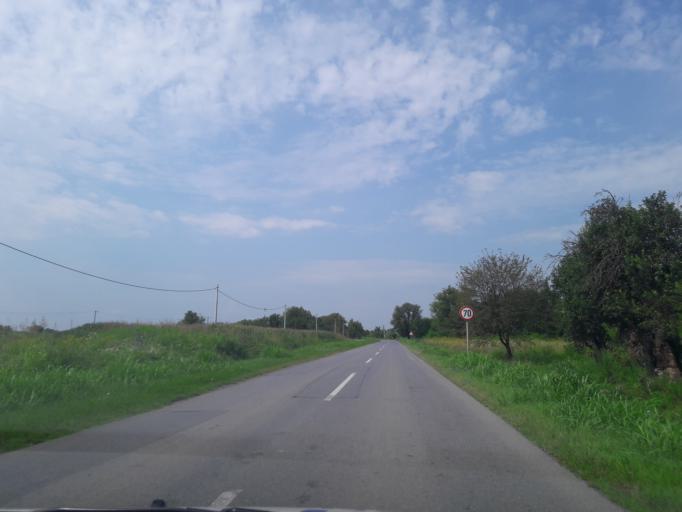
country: HR
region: Osjecko-Baranjska
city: Gorjani
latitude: 45.4925
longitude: 18.4082
